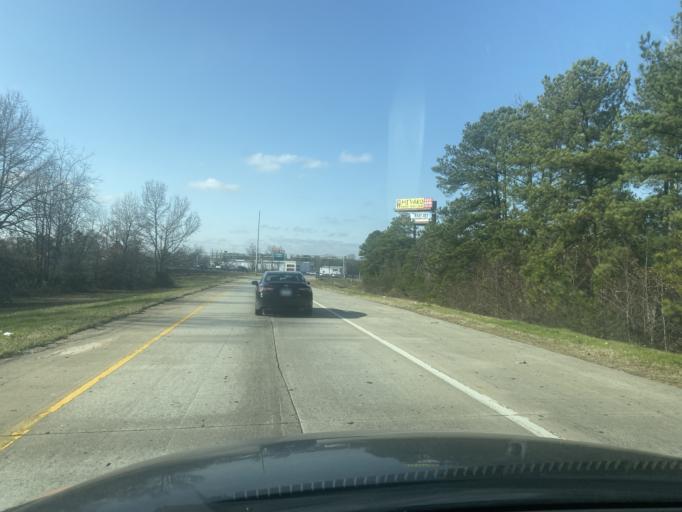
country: US
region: Georgia
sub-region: Henry County
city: McDonough
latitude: 33.4139
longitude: -84.1627
